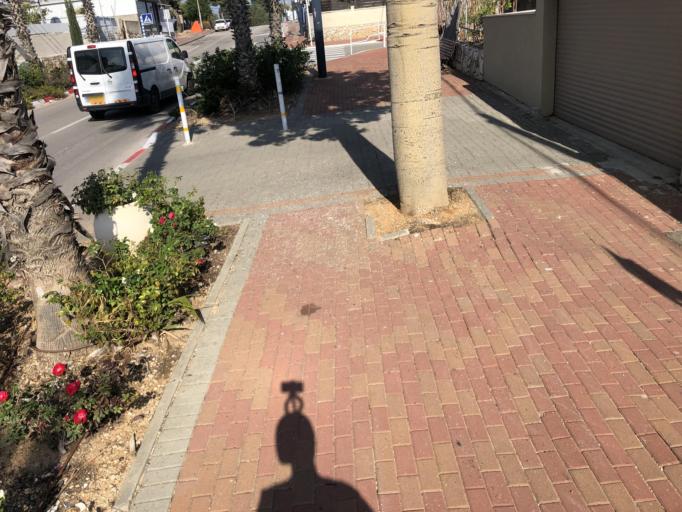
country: IL
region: Northern District
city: `Akko
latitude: 32.9345
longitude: 35.0918
